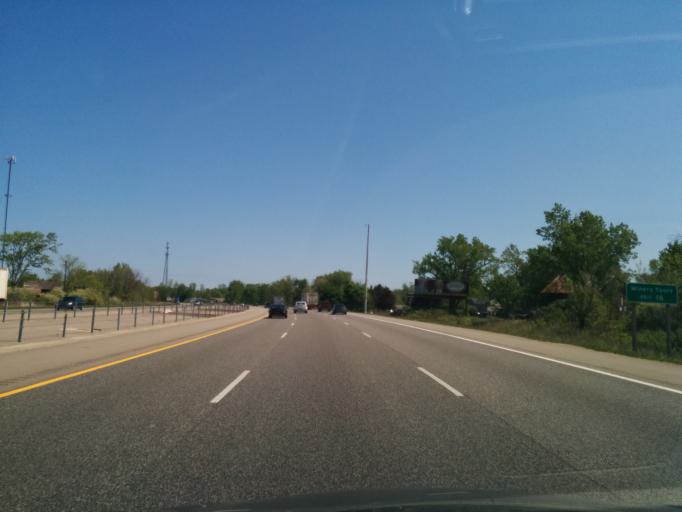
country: US
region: Michigan
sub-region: Berrien County
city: Bridgman
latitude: 41.9196
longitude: -86.5719
